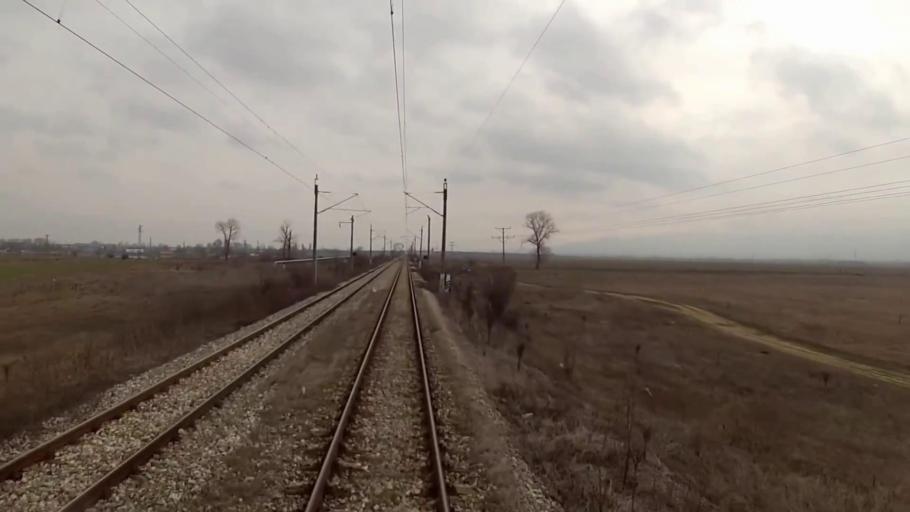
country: BG
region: Sofiya
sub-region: Obshtina Elin Pelin
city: Elin Pelin
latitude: 42.6506
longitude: 23.4834
